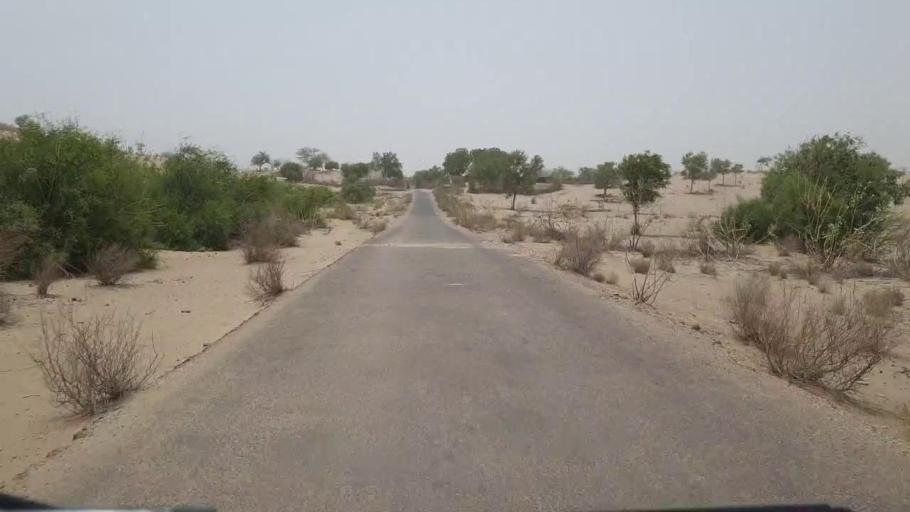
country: PK
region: Sindh
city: Naukot
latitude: 24.7828
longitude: 69.5327
